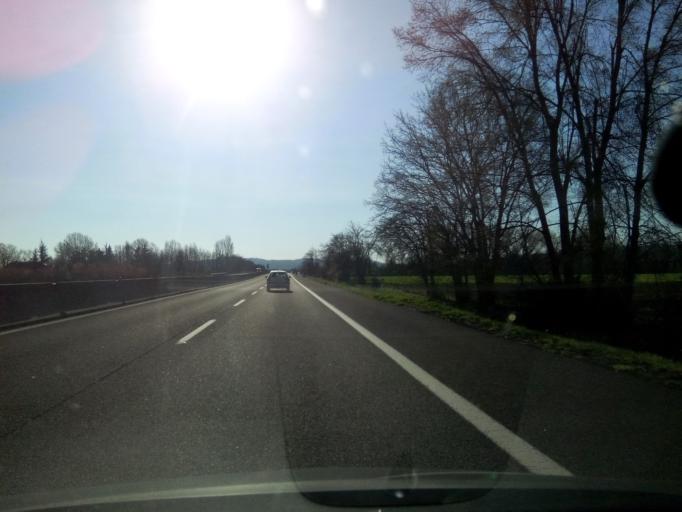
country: IT
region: Emilia-Romagna
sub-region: Provincia di Bologna
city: Zola Predosa
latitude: 44.4998
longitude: 11.2218
